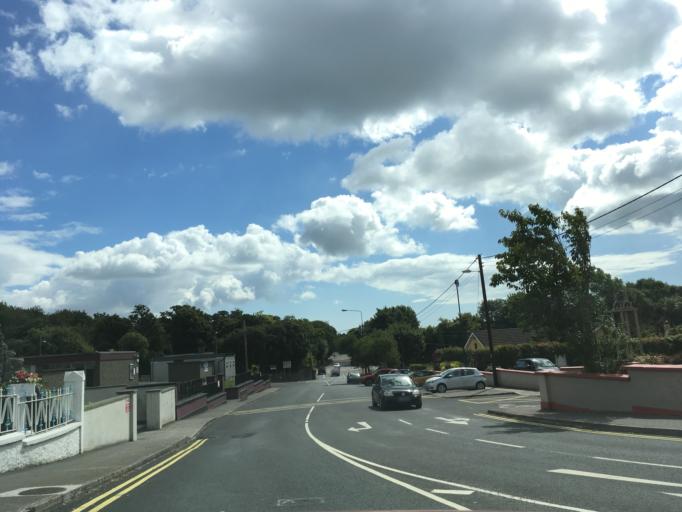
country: IE
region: Munster
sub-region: County Cork
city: Carrigaline
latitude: 51.8166
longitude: -8.3911
